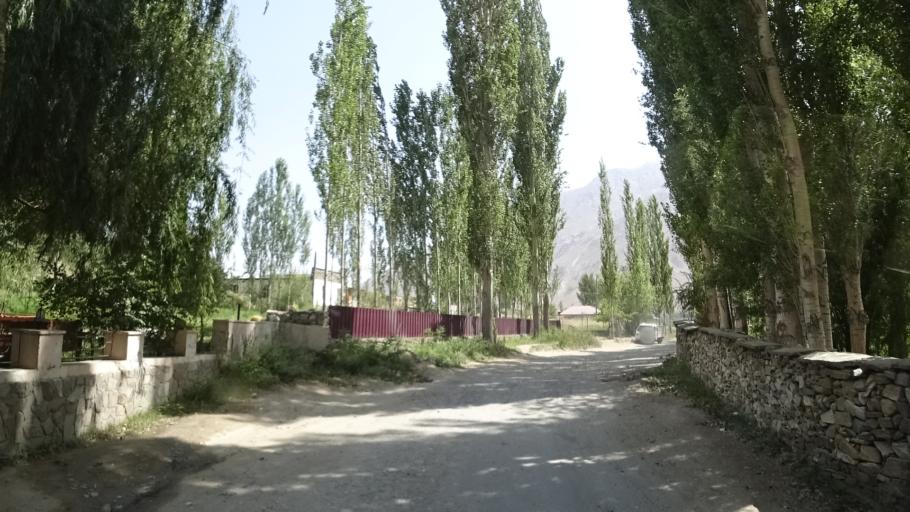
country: TJ
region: Gorno-Badakhshan
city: Ishqoshim
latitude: 36.9263
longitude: 71.4935
